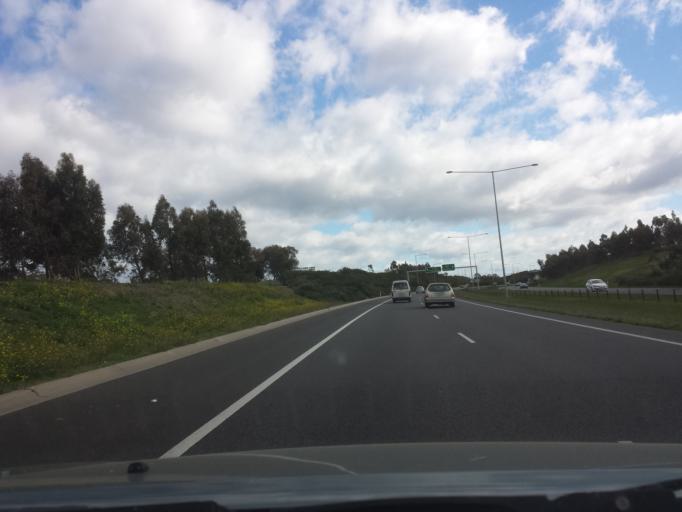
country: AU
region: Victoria
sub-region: Hume
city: Craigieburn
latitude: -37.6031
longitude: 144.9655
